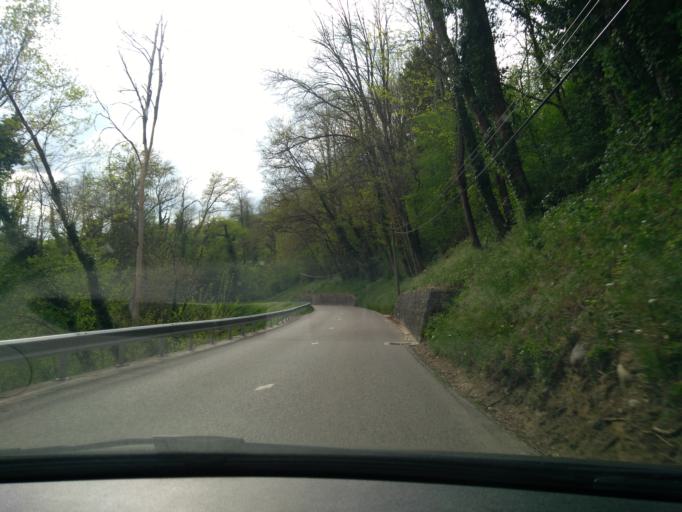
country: FR
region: Rhone-Alpes
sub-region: Departement de la Haute-Savoie
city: Rumilly
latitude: 45.8459
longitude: 5.9190
